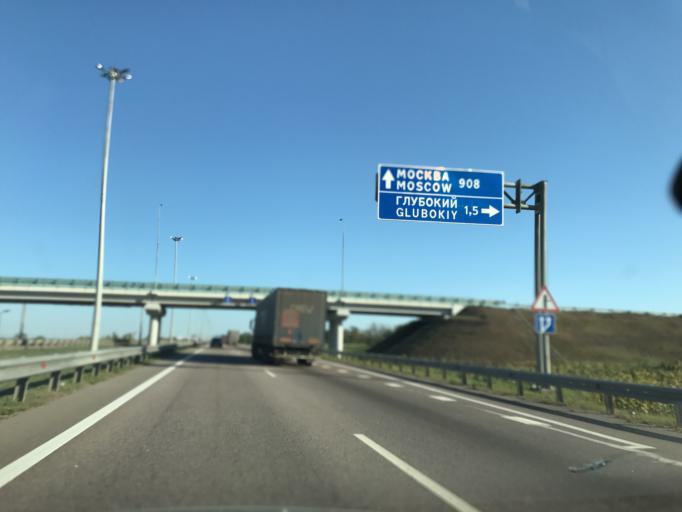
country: RU
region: Rostov
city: Glubokiy
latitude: 48.5006
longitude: 40.3410
